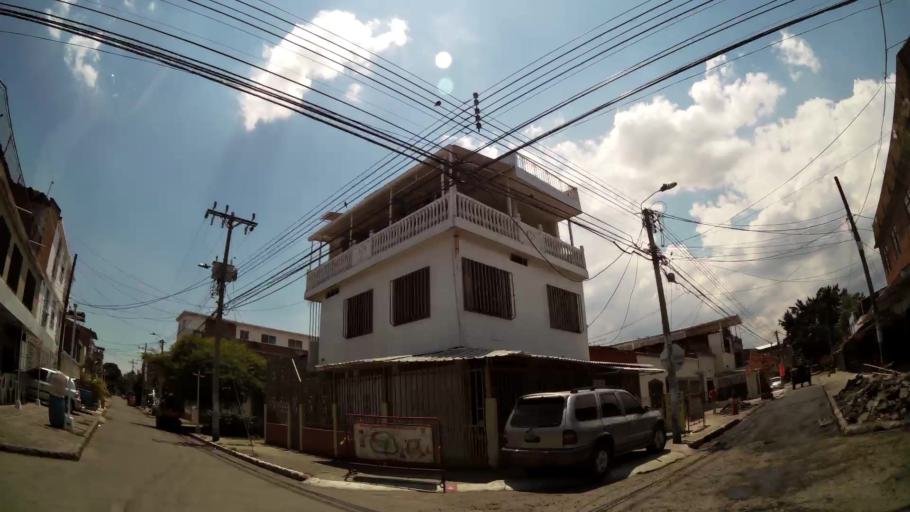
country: CO
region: Valle del Cauca
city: Cali
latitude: 3.4454
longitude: -76.4971
